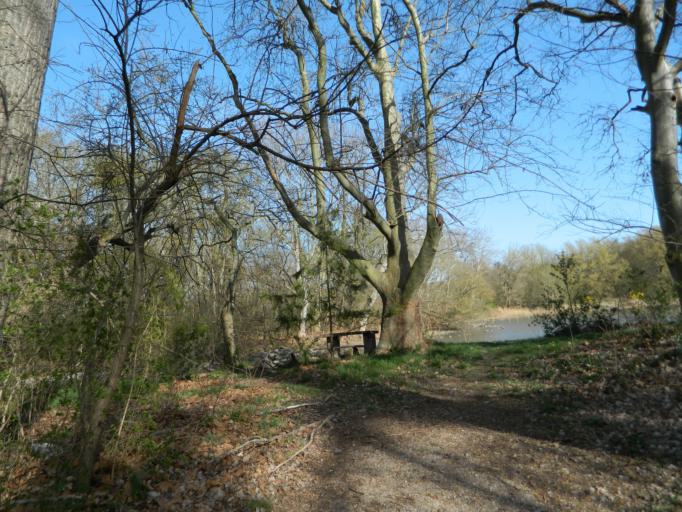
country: HU
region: Fejer
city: Pakozd
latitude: 47.2299
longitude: 18.4905
